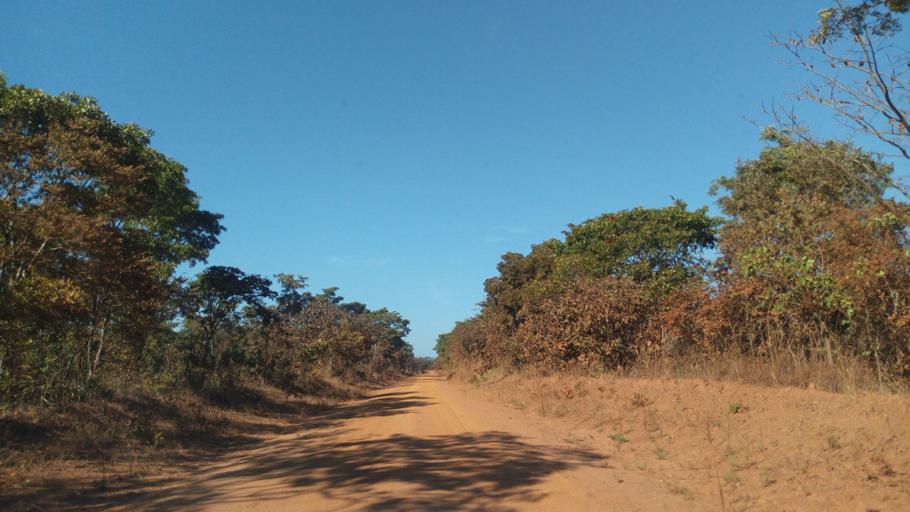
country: ZM
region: Luapula
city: Mwense
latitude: -10.6515
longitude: 28.4088
